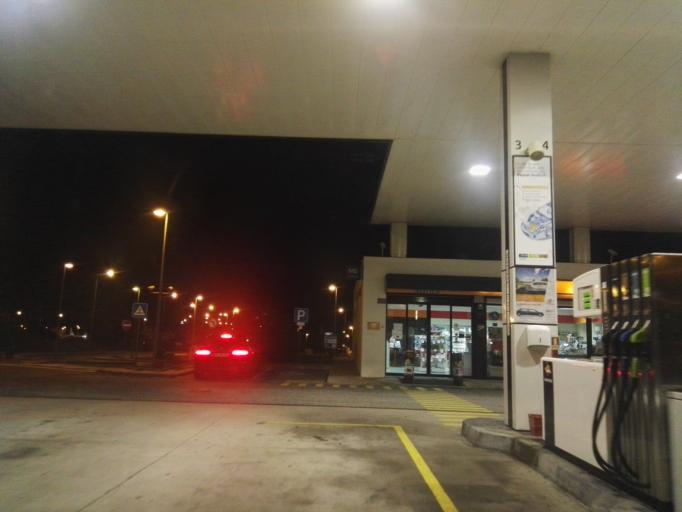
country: PT
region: Evora
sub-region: Vendas Novas
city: Vendas Novas
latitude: 38.6227
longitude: -8.5775
